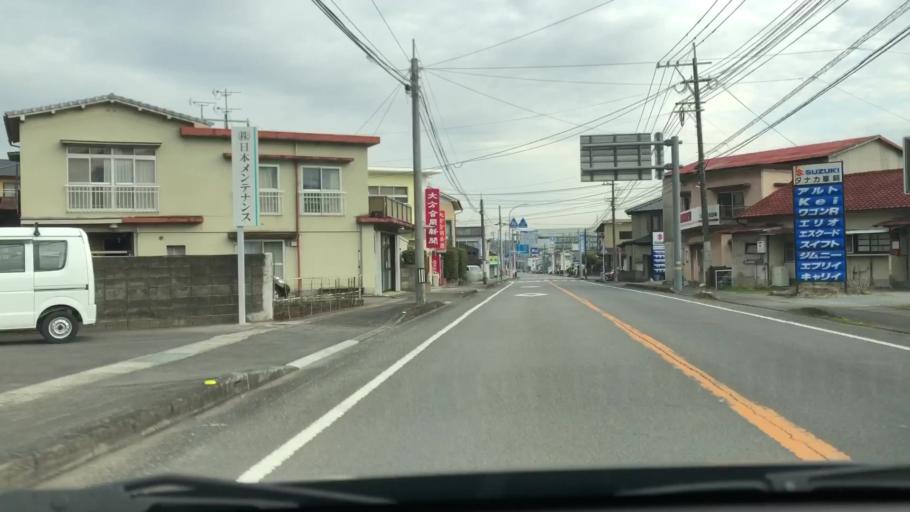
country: JP
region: Oita
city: Takedamachi
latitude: 32.9741
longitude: 131.5799
